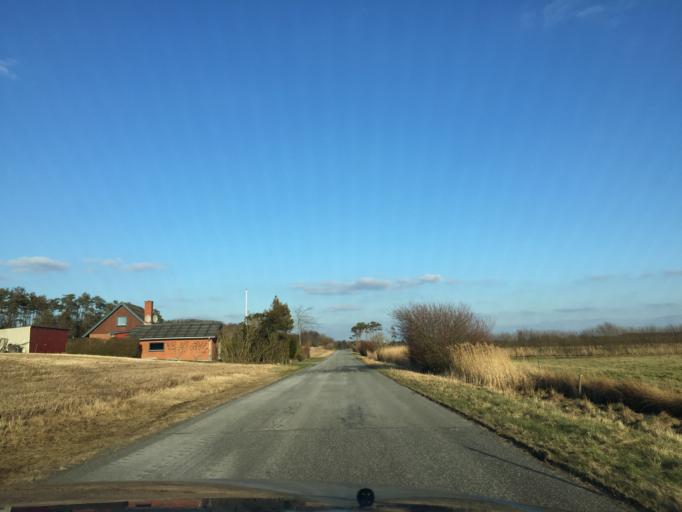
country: DK
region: Central Jutland
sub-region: Holstebro Kommune
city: Vinderup
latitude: 56.5747
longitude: 8.7969
